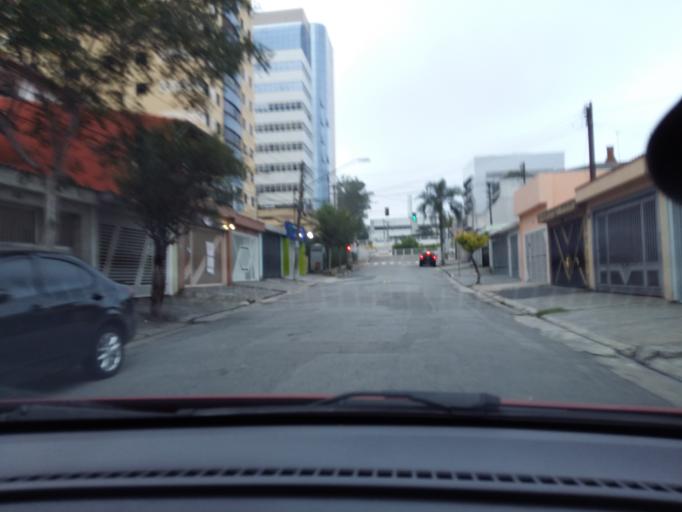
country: BR
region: Sao Paulo
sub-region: Sao Caetano Do Sul
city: Sao Caetano do Sul
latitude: -23.6397
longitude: -46.5952
